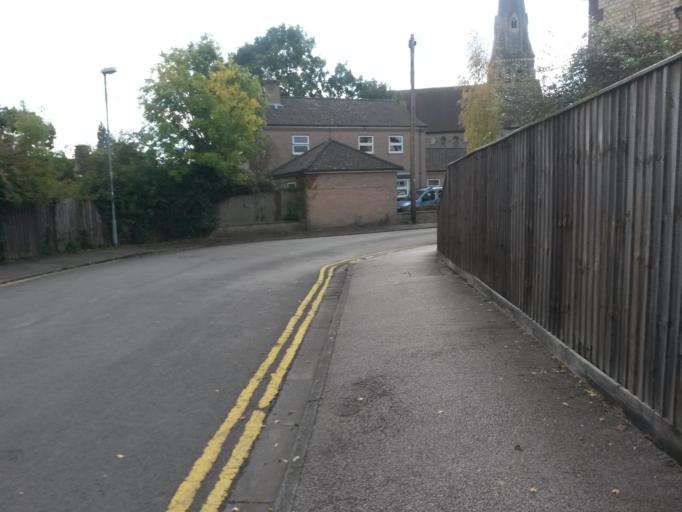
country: GB
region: England
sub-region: Cambridgeshire
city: Cambridge
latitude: 52.2165
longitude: 0.1167
